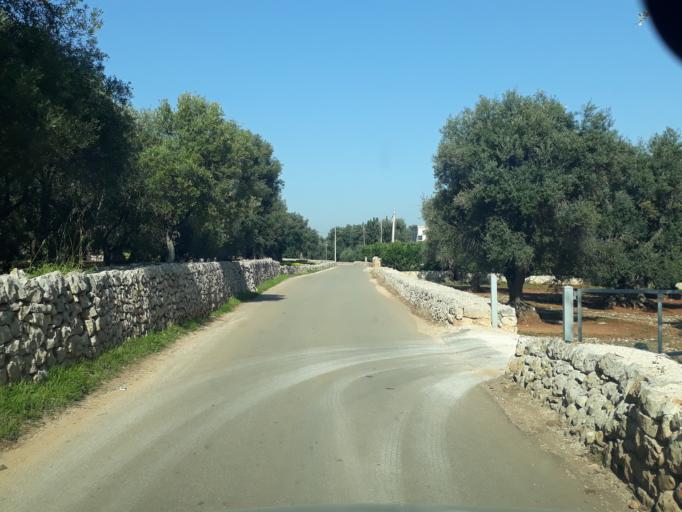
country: IT
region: Apulia
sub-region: Provincia di Brindisi
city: Fasano
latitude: 40.8416
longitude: 17.3453
